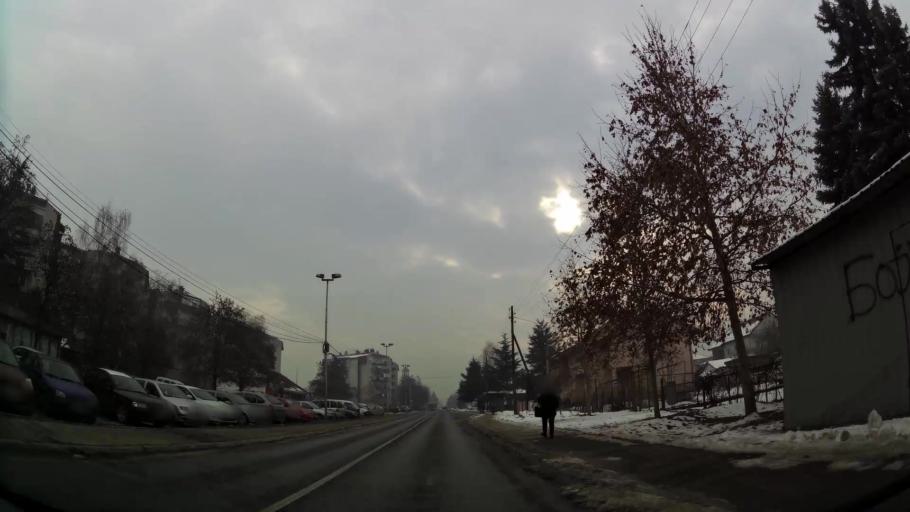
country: MK
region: Saraj
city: Saraj
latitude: 42.0201
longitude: 21.3529
